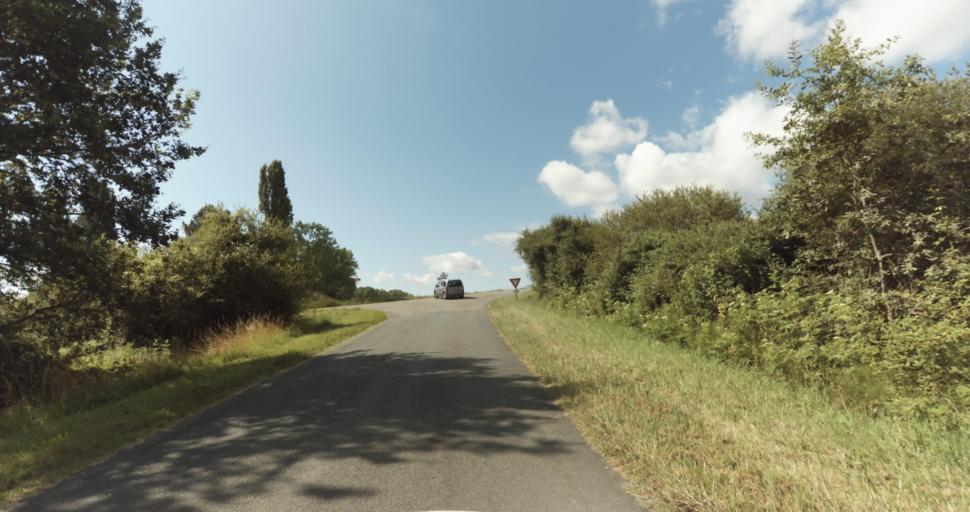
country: FR
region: Aquitaine
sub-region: Departement de la Gironde
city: Bazas
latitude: 44.4430
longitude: -0.1714
